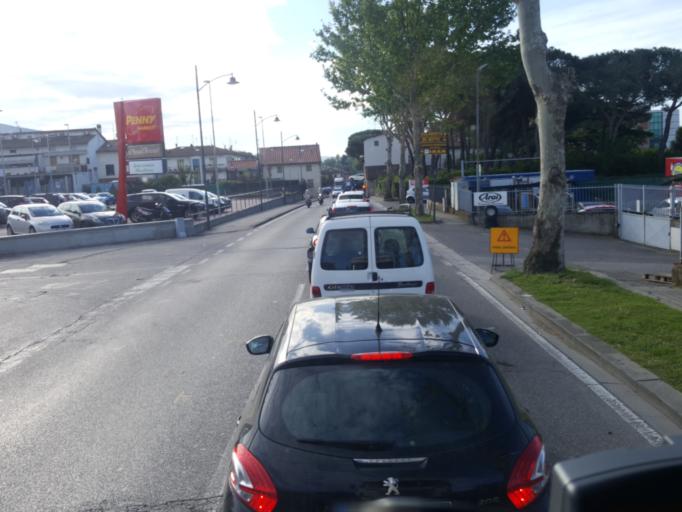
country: IT
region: Tuscany
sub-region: Province of Florence
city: Calenzano
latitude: 43.8470
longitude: 11.1756
